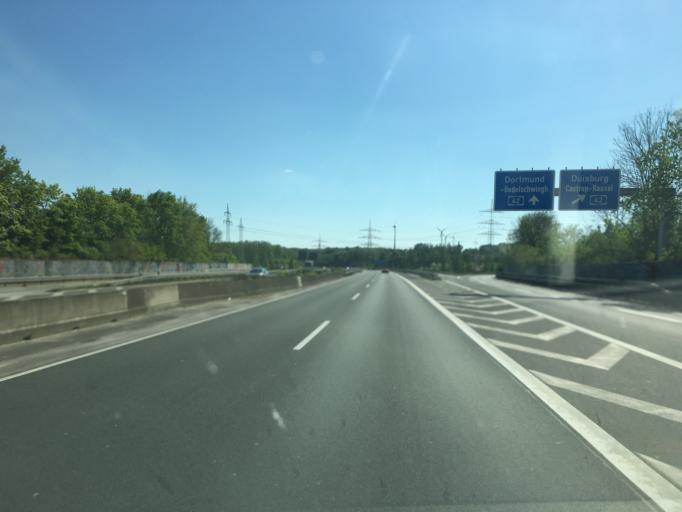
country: DE
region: North Rhine-Westphalia
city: Castrop-Rauxel
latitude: 51.5651
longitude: 7.3596
